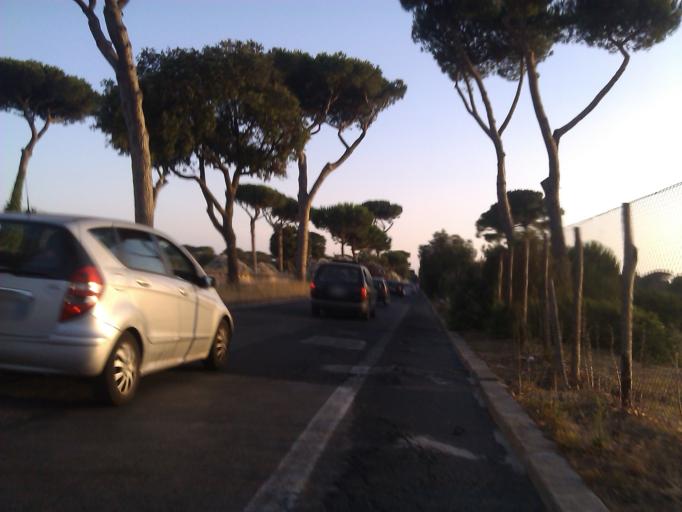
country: IT
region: Latium
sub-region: Citta metropolitana di Roma Capitale
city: Acilia-Castel Fusano-Ostia Antica
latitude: 41.7265
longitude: 12.3324
